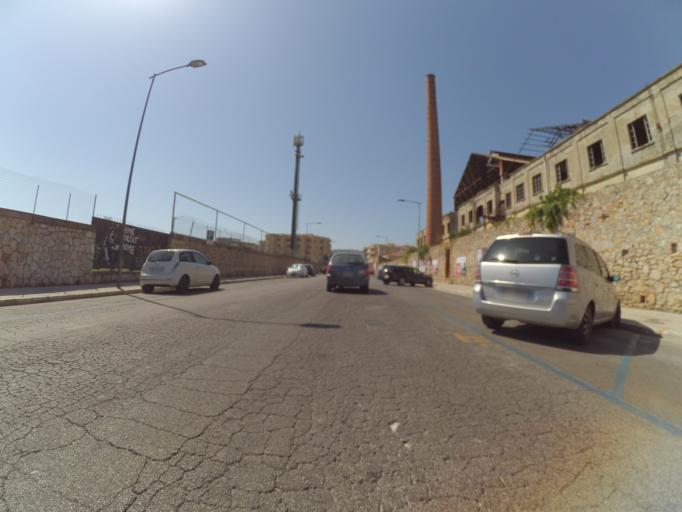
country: IT
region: Latium
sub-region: Provincia di Latina
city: Gaeta
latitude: 41.2117
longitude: 13.5675
